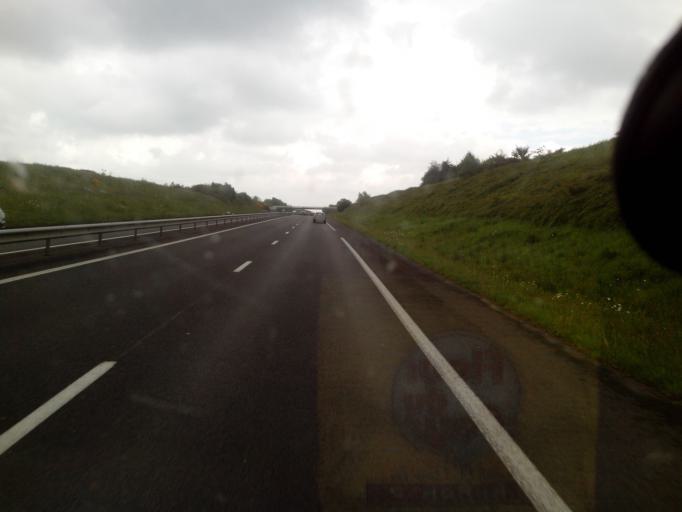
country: FR
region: Lower Normandy
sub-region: Departement de la Manche
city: Saint-Amand
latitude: 48.9976
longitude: -0.9140
